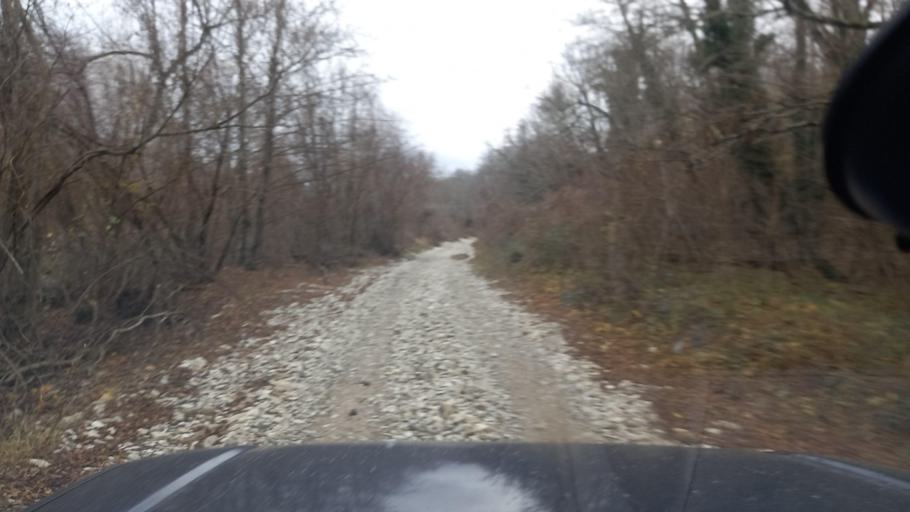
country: RU
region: Krasnodarskiy
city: Pshada
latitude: 44.4941
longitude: 38.4211
